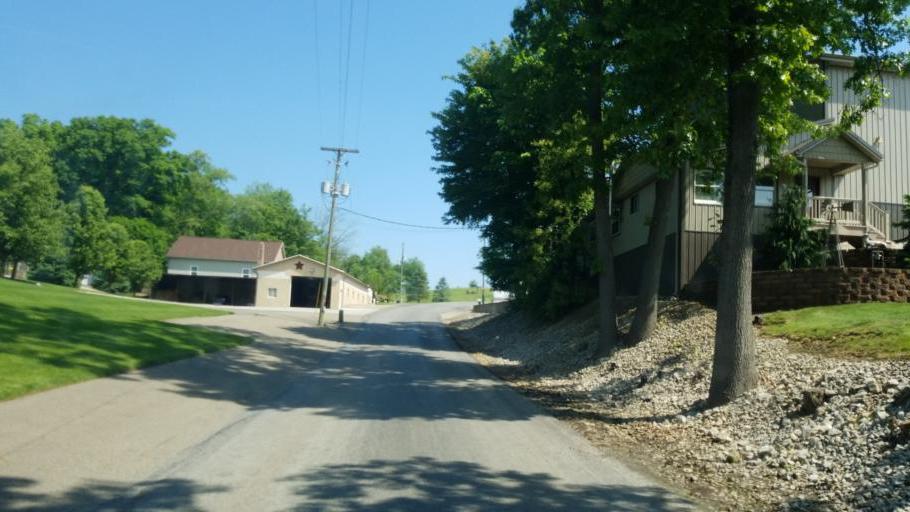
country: US
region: Ohio
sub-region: Tuscarawas County
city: Sugarcreek
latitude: 40.5146
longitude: -81.7809
